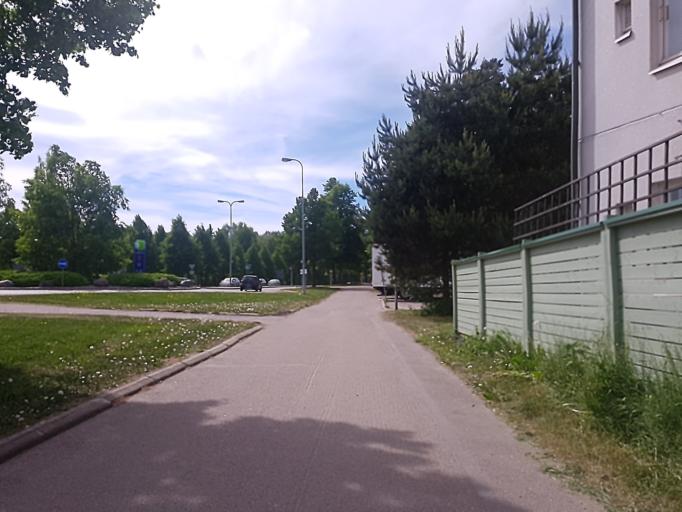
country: FI
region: Uusimaa
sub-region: Helsinki
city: Teekkarikylae
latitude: 60.2766
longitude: 24.8576
